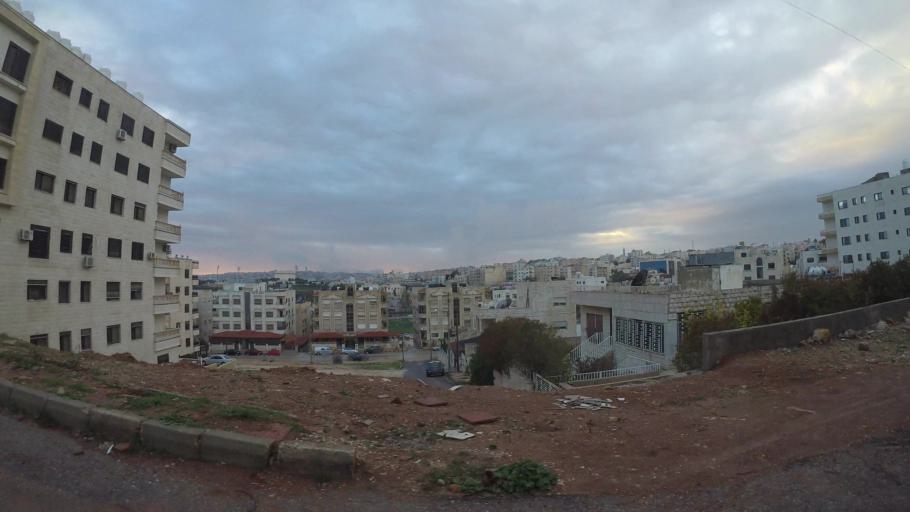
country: JO
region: Amman
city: Amman
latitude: 31.9881
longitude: 35.9128
